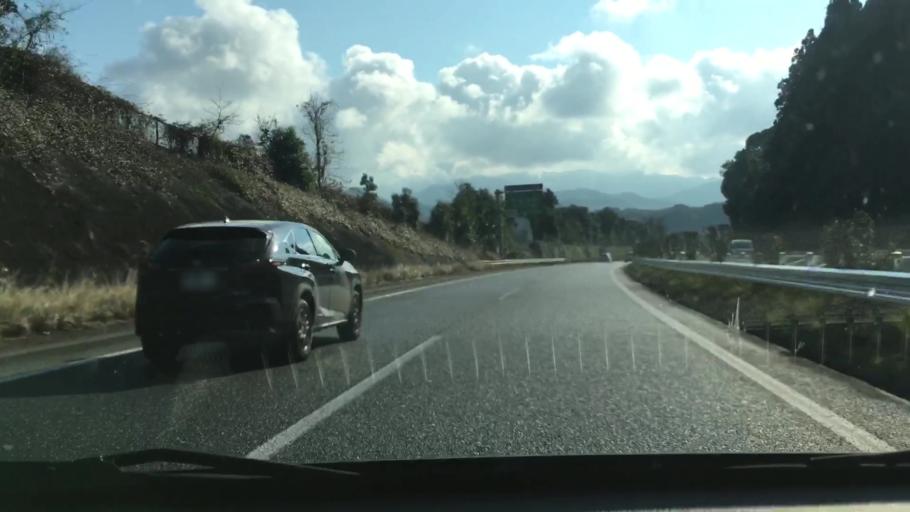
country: JP
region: Kumamoto
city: Matsubase
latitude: 32.5862
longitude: 130.7167
